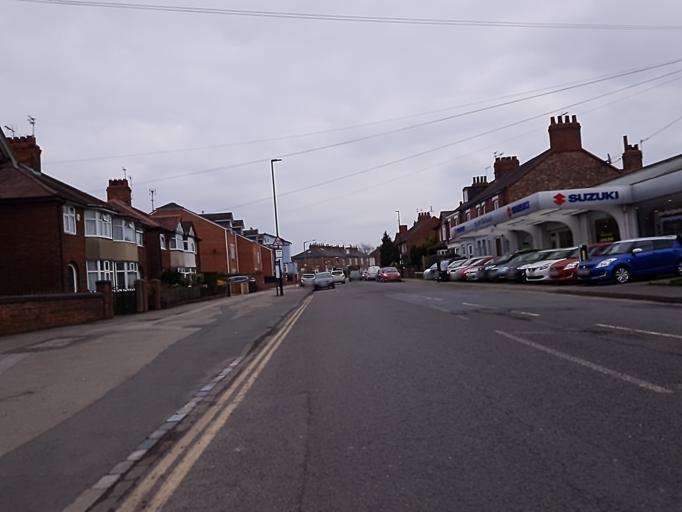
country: GB
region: England
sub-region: City of York
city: York
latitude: 53.9644
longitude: -1.0683
